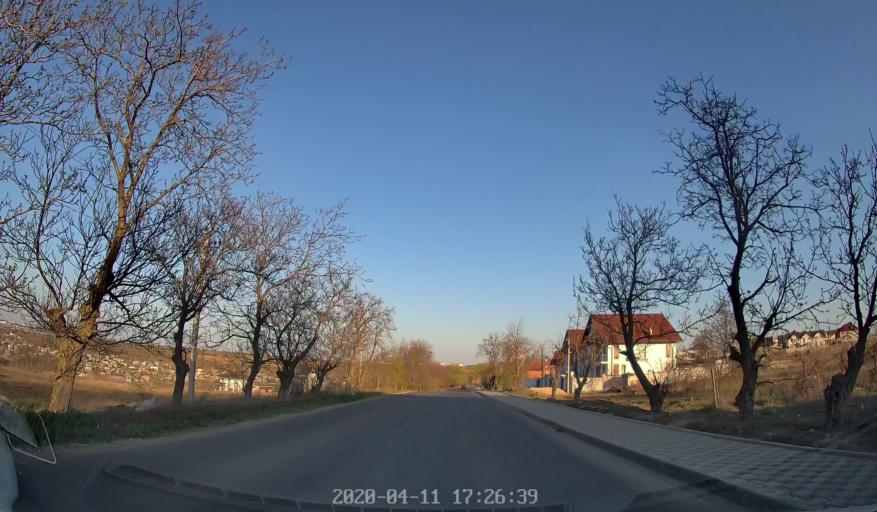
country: MD
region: Chisinau
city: Vatra
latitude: 47.0125
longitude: 28.7572
